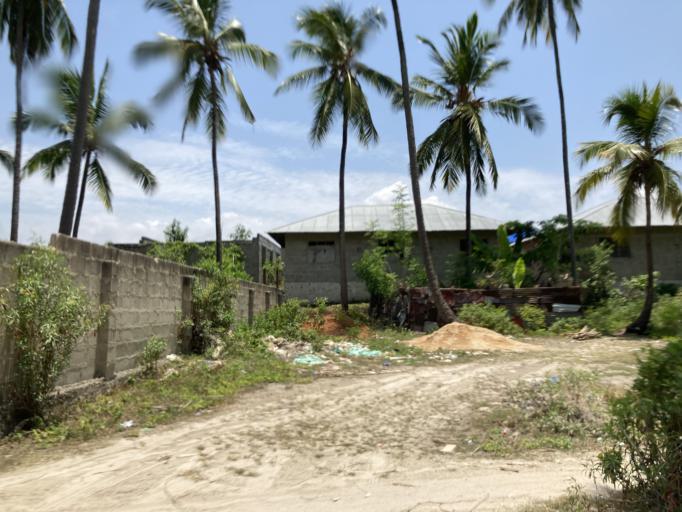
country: TZ
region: Zanzibar North
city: Gamba
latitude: -5.9266
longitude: 39.3581
